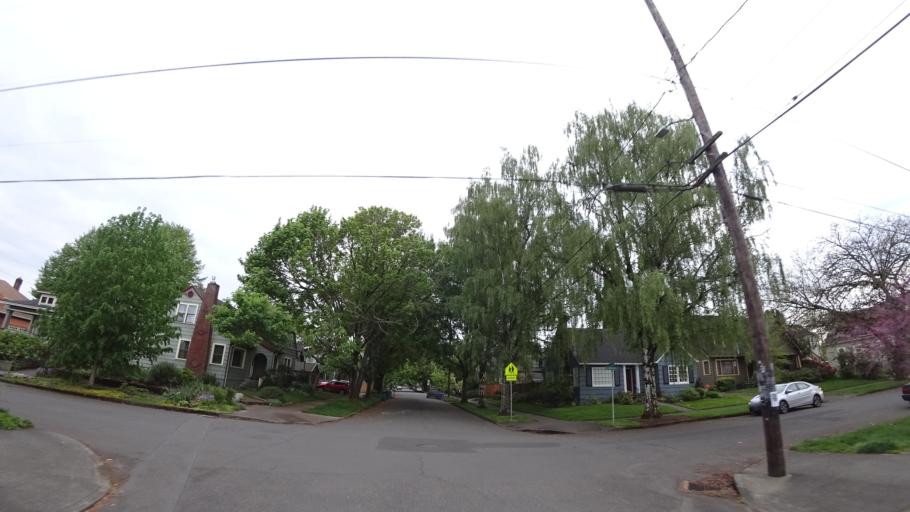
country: US
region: Oregon
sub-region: Clackamas County
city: Milwaukie
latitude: 45.4787
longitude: -122.6518
